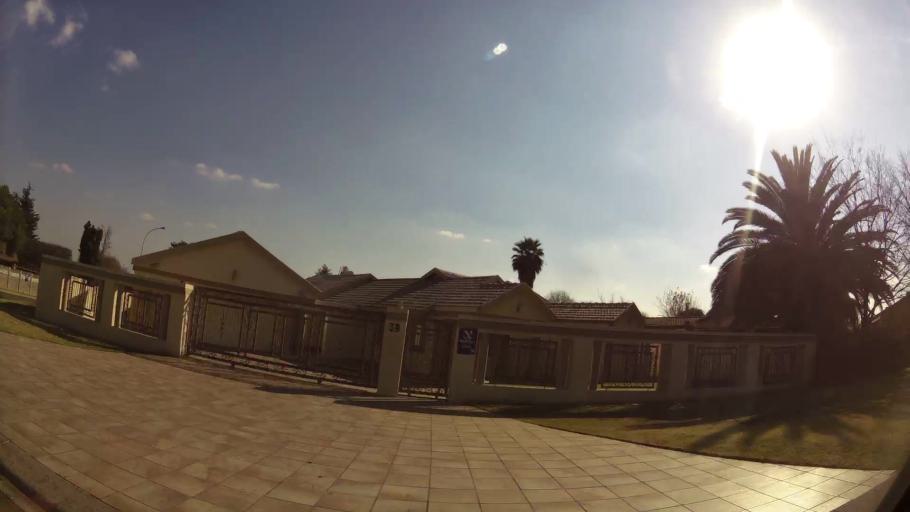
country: ZA
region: Gauteng
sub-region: Ekurhuleni Metropolitan Municipality
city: Benoni
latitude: -26.2431
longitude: 28.3139
